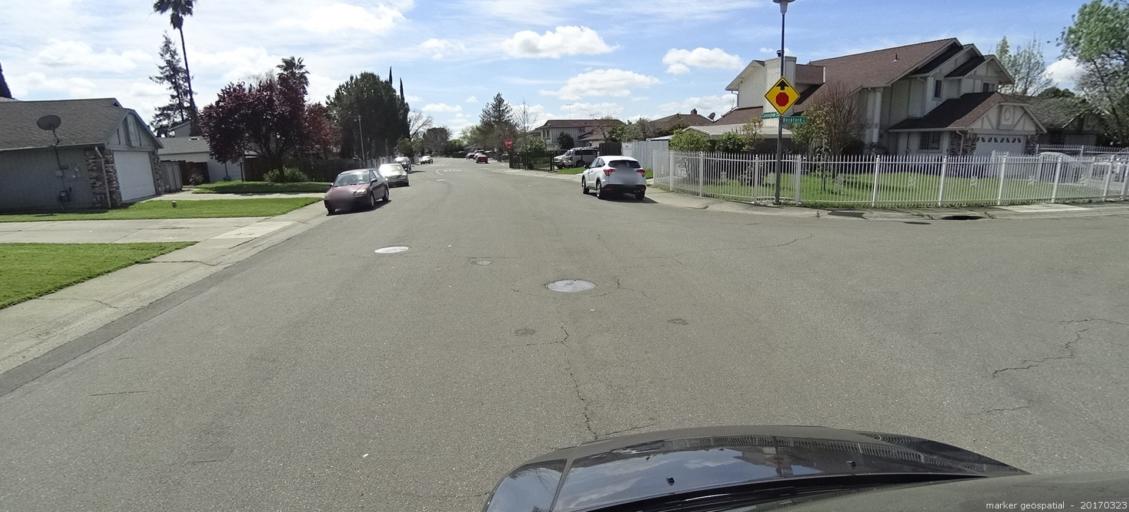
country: US
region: California
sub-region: Sacramento County
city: Florin
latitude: 38.5066
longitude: -121.4266
